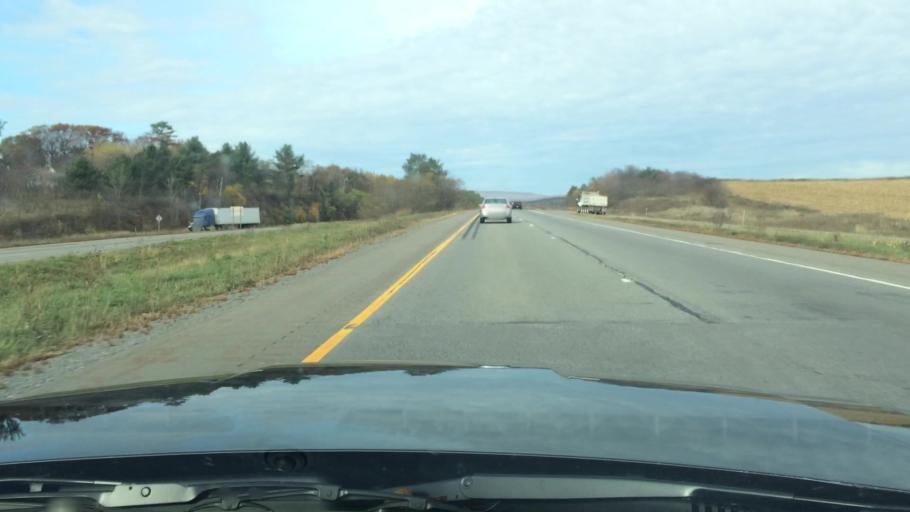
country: US
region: Wisconsin
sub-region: Marathon County
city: Mosinee
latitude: 44.7874
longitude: -89.6803
